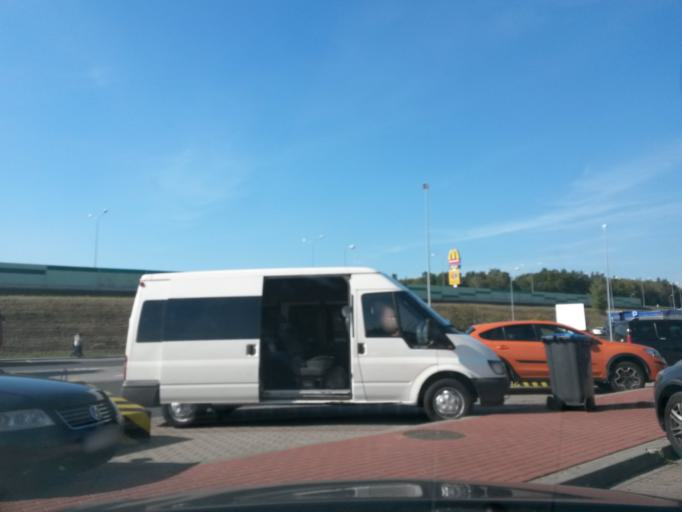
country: PL
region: Silesian Voivodeship
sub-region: Powiat gliwicki
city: Sosnicowice
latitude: 50.3111
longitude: 18.5521
